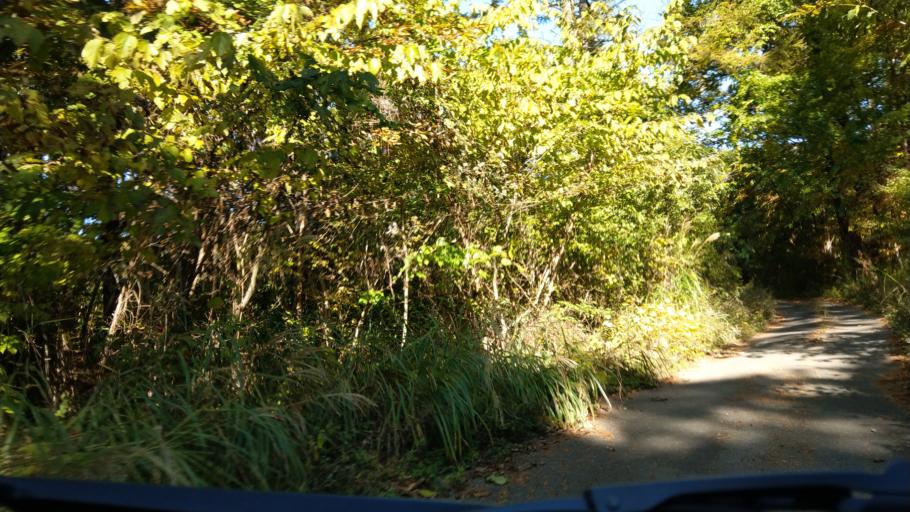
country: JP
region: Nagano
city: Komoro
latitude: 36.3690
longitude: 138.4439
